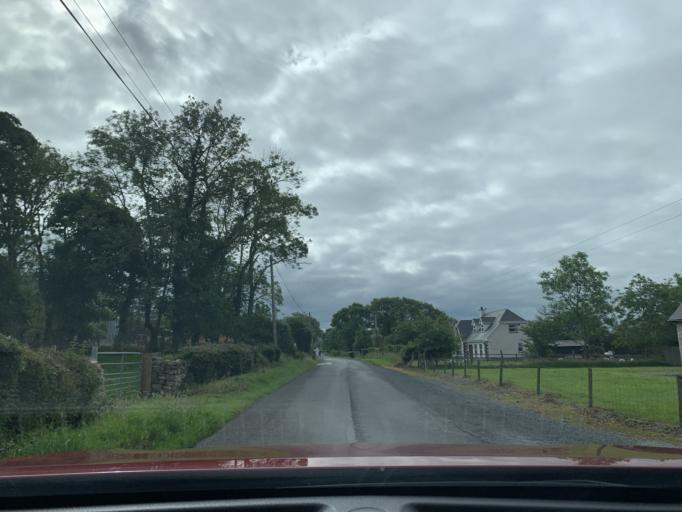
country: IE
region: Connaught
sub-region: Sligo
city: Sligo
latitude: 54.3417
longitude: -8.4843
